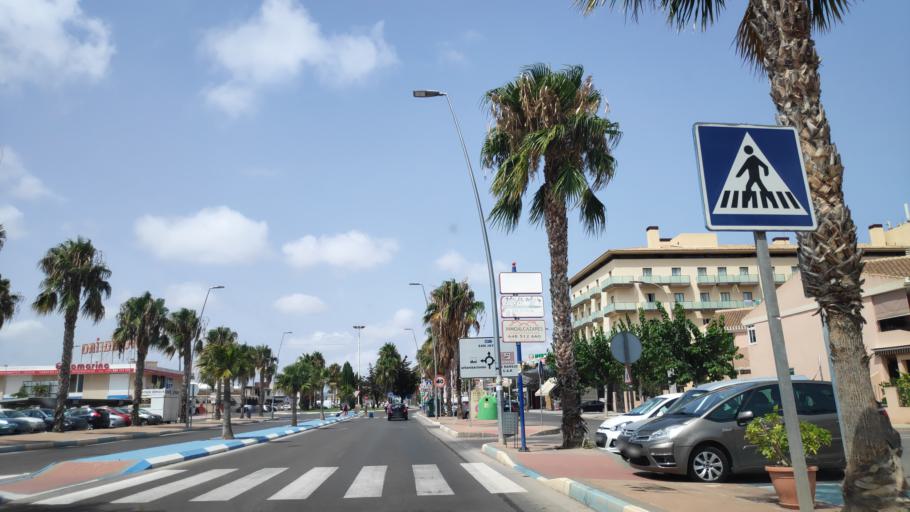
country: ES
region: Murcia
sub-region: Murcia
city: Los Alcazares
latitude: 37.7536
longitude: -0.8468
